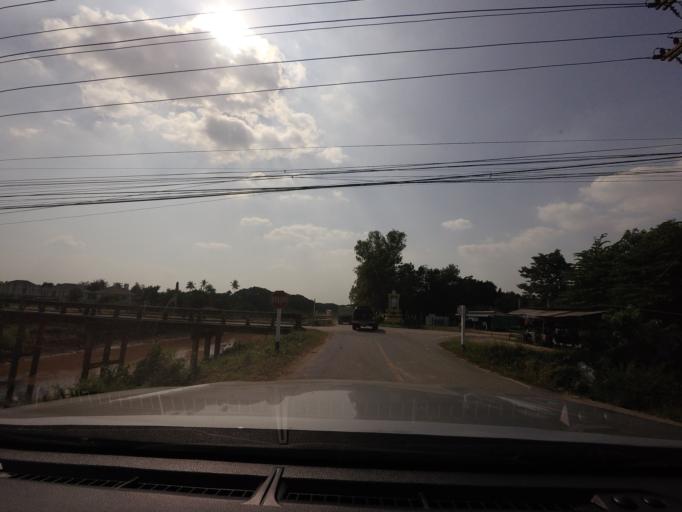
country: TH
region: Phitsanulok
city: Phitsanulok
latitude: 16.8066
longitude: 100.2166
